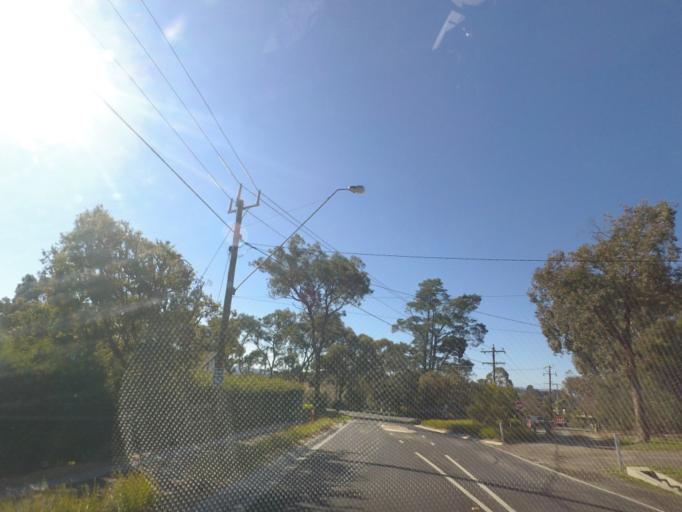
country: AU
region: Victoria
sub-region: Manningham
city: Warrandyte
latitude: -37.7364
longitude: 145.2711
